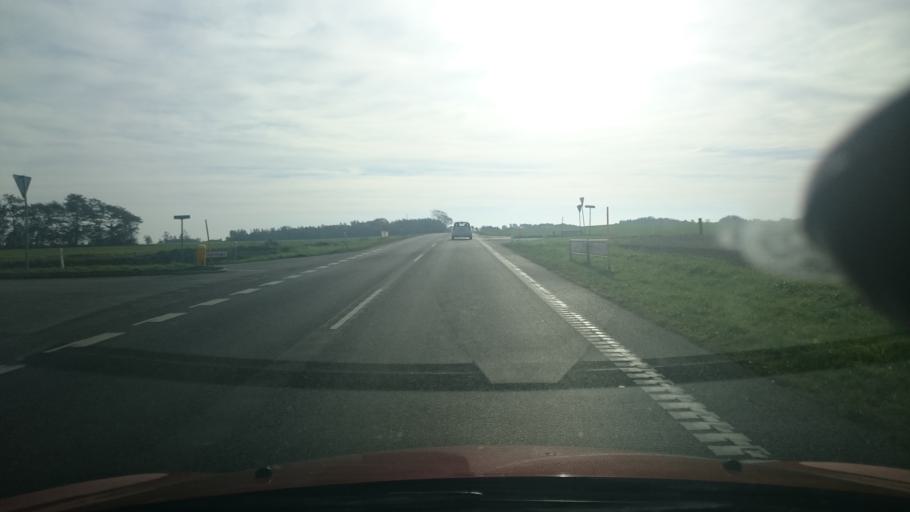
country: DK
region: Central Jutland
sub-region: Randers Kommune
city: Assentoft
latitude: 56.4160
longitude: 10.2177
